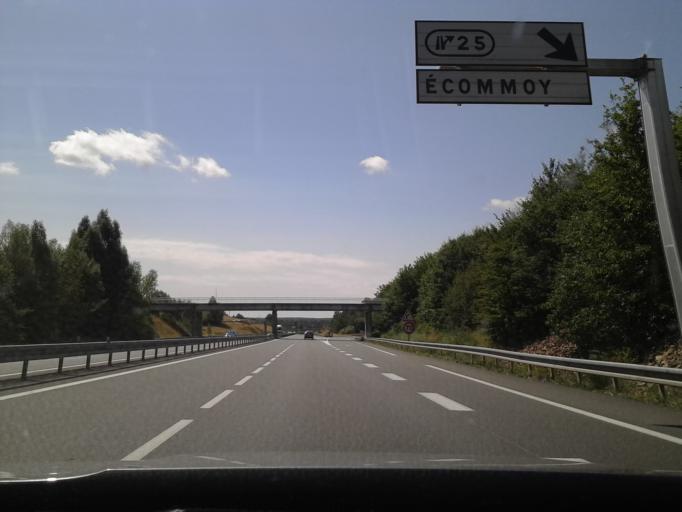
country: FR
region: Pays de la Loire
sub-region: Departement de la Sarthe
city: Ecommoy
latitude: 47.8248
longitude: 0.3066
